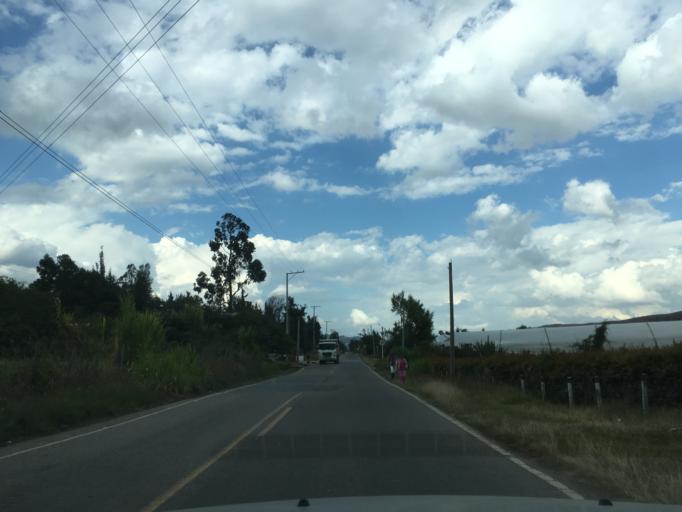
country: CO
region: Boyaca
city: Sutamarchan
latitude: 5.5845
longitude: -73.6425
